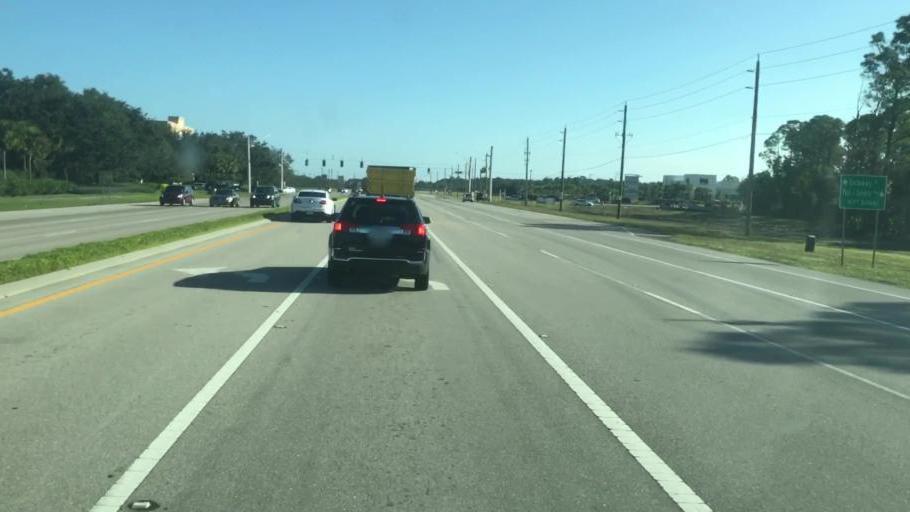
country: US
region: Florida
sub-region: Lee County
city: Gateway
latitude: 26.5552
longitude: -81.7519
